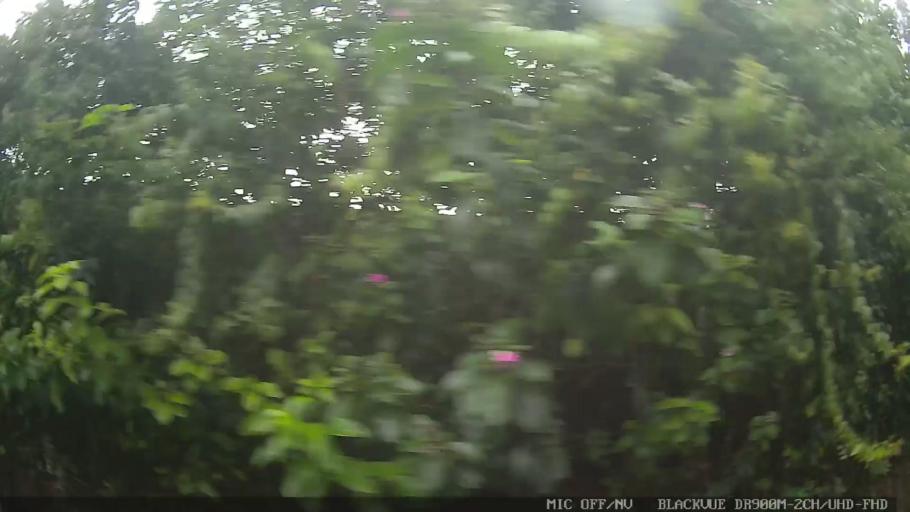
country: BR
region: Sao Paulo
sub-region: Suzano
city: Suzano
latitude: -23.6431
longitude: -46.2901
